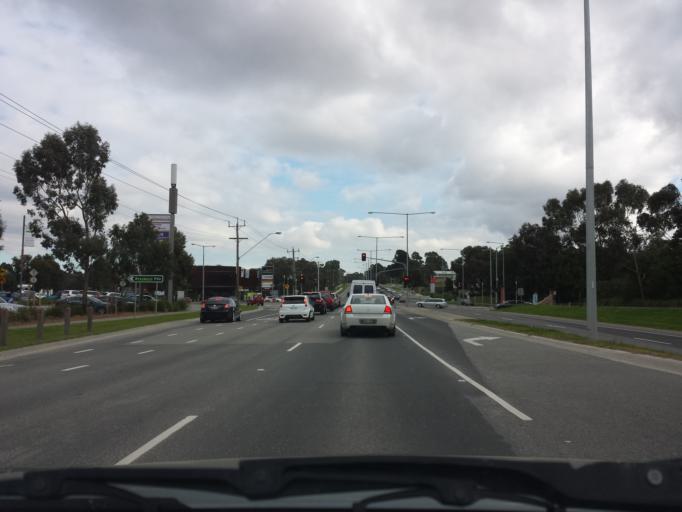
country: AU
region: Victoria
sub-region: Knox
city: Rowville
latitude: -37.9274
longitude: 145.2530
